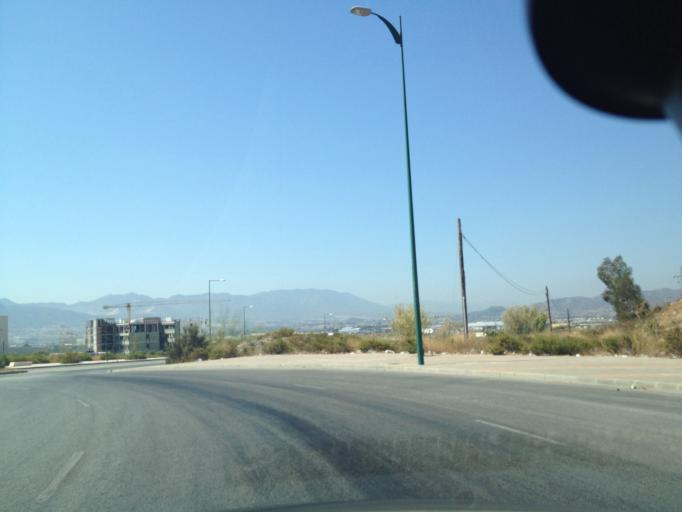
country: ES
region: Andalusia
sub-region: Provincia de Malaga
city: Malaga
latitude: 36.7210
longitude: -4.4958
